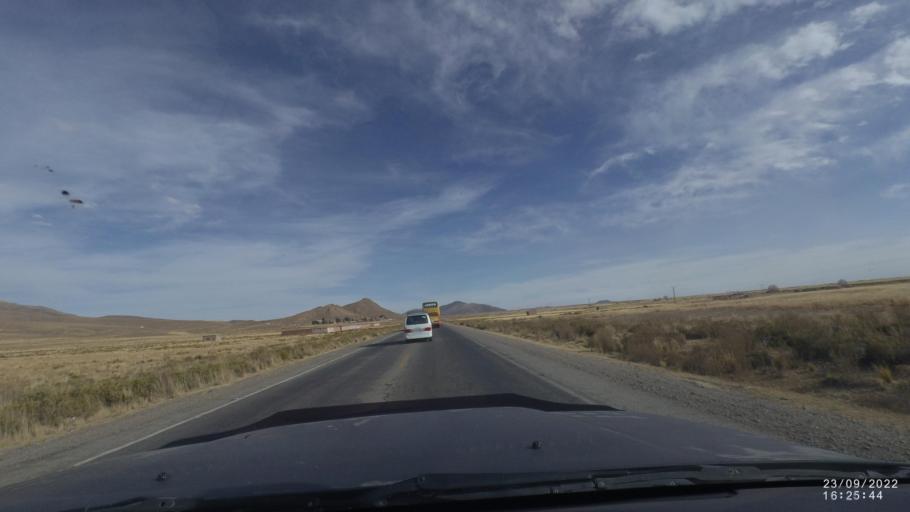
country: BO
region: Oruro
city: Machacamarca
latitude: -18.0958
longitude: -67.0094
